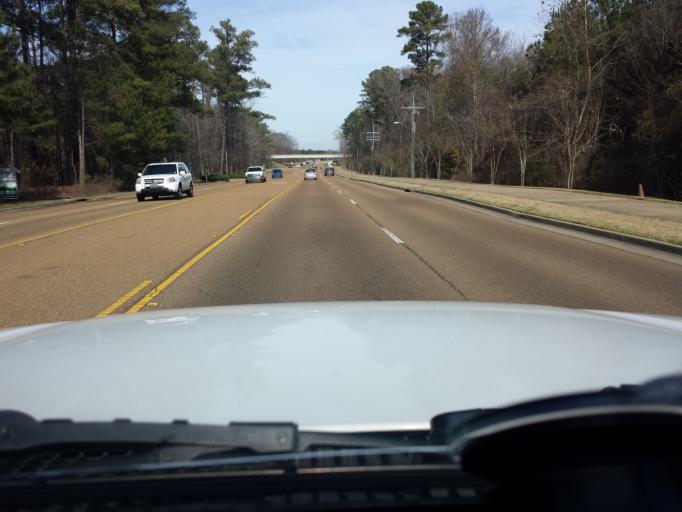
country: US
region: Mississippi
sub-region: Madison County
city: Ridgeland
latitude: 32.4232
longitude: -90.1063
